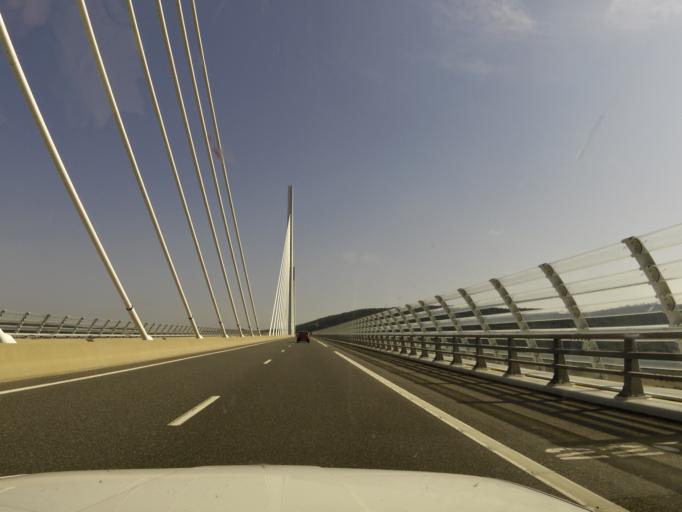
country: FR
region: Midi-Pyrenees
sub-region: Departement de l'Aveyron
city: Creissels
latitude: 44.0884
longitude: 3.0214
